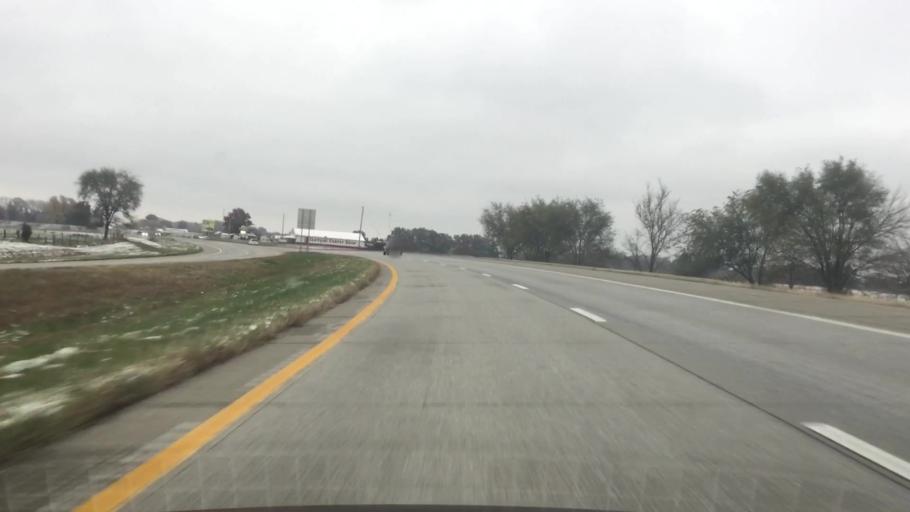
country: US
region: Missouri
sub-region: Henry County
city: Clinton
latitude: 38.3902
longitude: -93.8227
